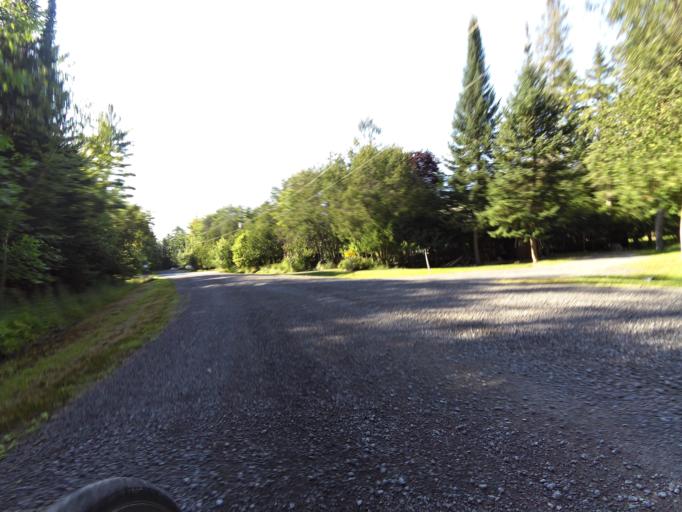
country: CA
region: Ontario
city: Bells Corners
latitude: 45.4813
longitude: -76.0232
